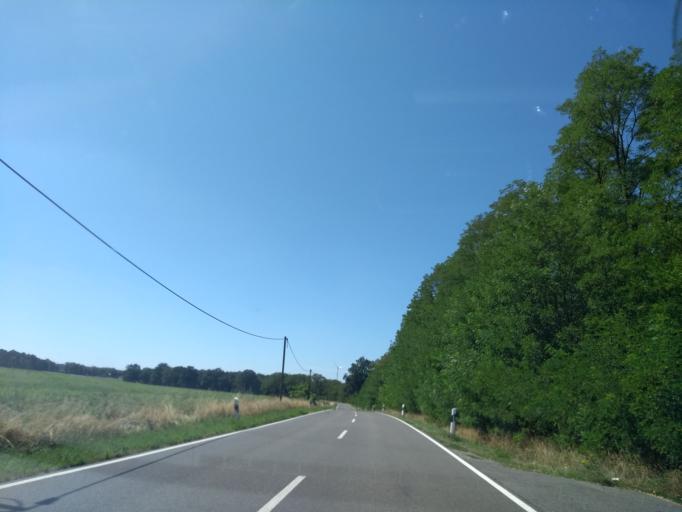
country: DE
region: Brandenburg
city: Bronkow
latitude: 51.6616
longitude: 13.9054
